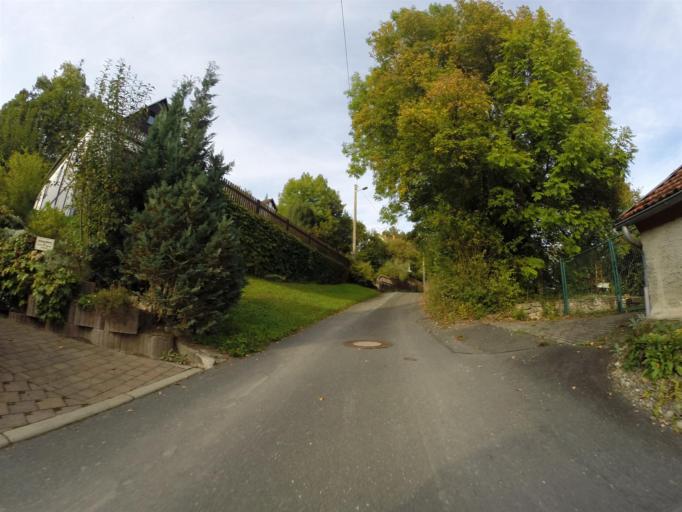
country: DE
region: Thuringia
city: Lehesten
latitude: 50.9608
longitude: 11.6135
